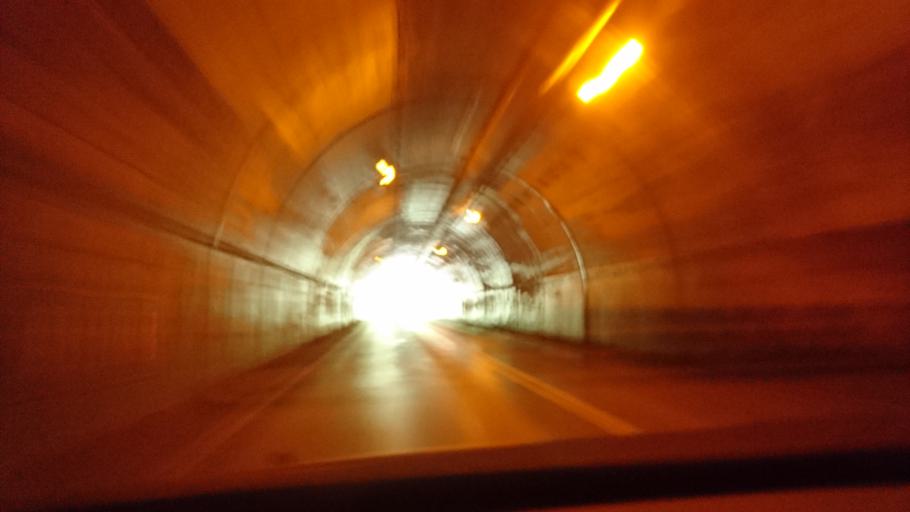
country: JP
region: Iwate
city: Otsuchi
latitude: 39.3982
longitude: 141.9499
